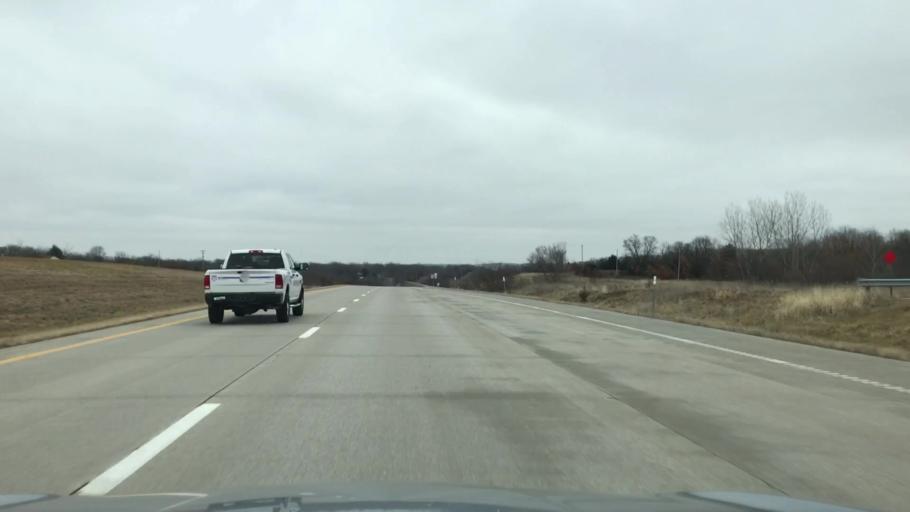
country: US
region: Missouri
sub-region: Linn County
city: Marceline
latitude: 39.7652
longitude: -92.7428
